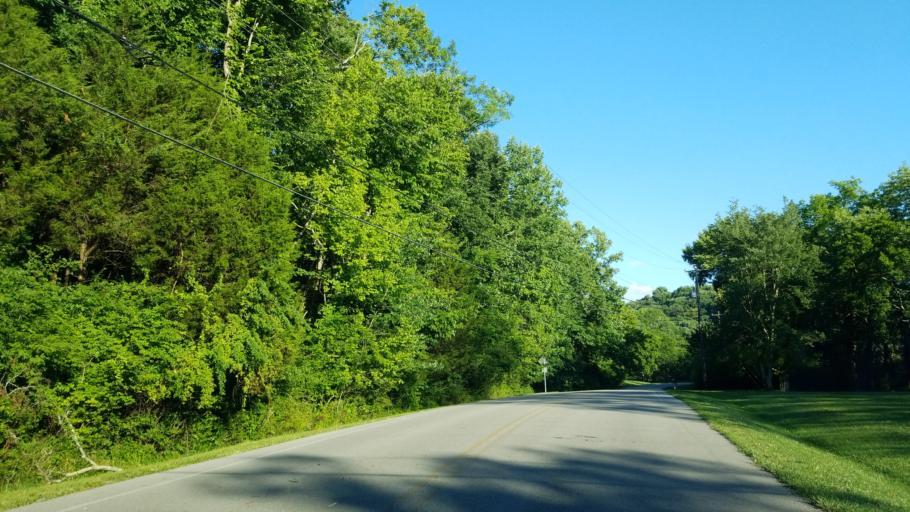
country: US
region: Tennessee
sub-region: Williamson County
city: Brentwood
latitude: 36.0506
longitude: -86.7918
